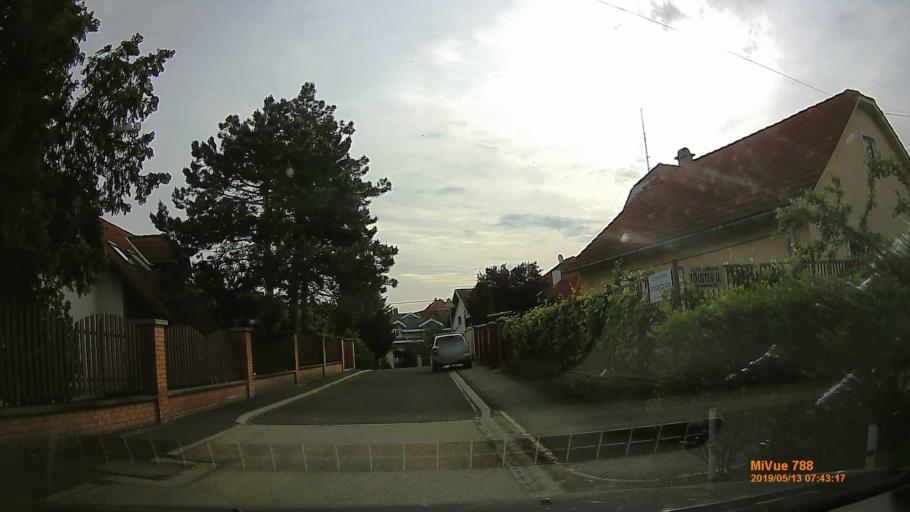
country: HU
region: Budapest
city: Budapest XXIII. keruelet
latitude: 47.4099
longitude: 19.0935
